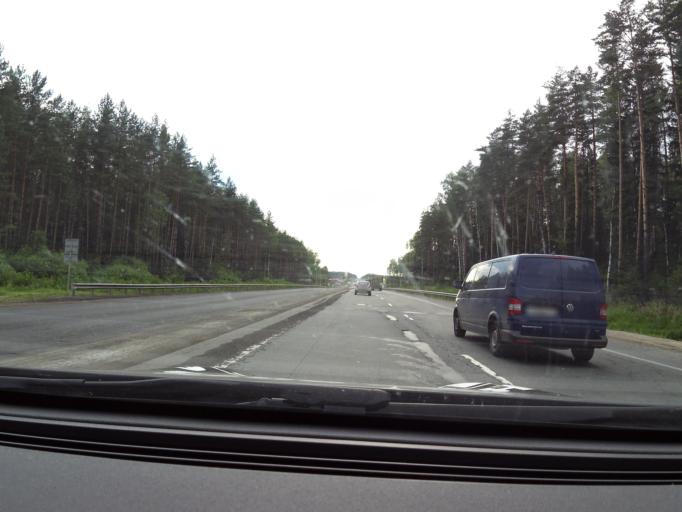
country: RU
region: Vladimir
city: Luknovo
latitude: 56.2370
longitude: 41.9642
